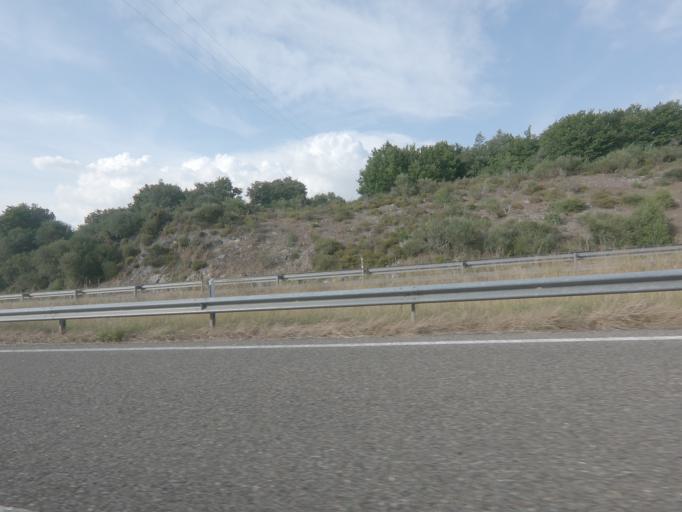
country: ES
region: Galicia
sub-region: Provincia de Ourense
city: Xinzo de Limia
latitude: 42.0679
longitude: -7.7034
